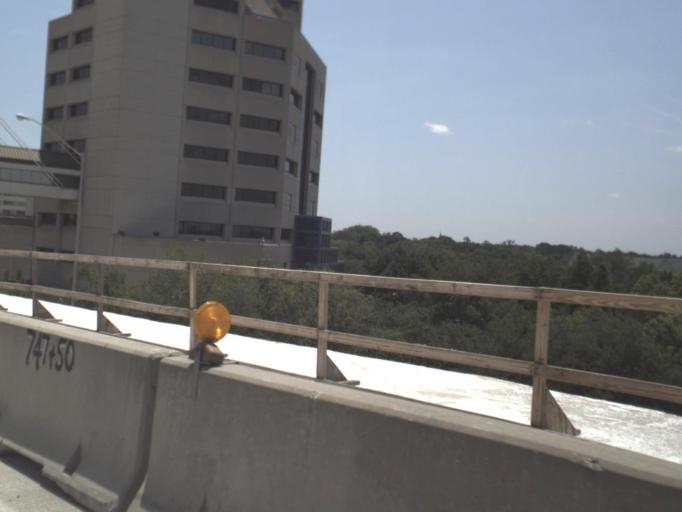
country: US
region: Florida
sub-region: Duval County
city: Jacksonville
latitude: 30.3139
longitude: -81.6646
